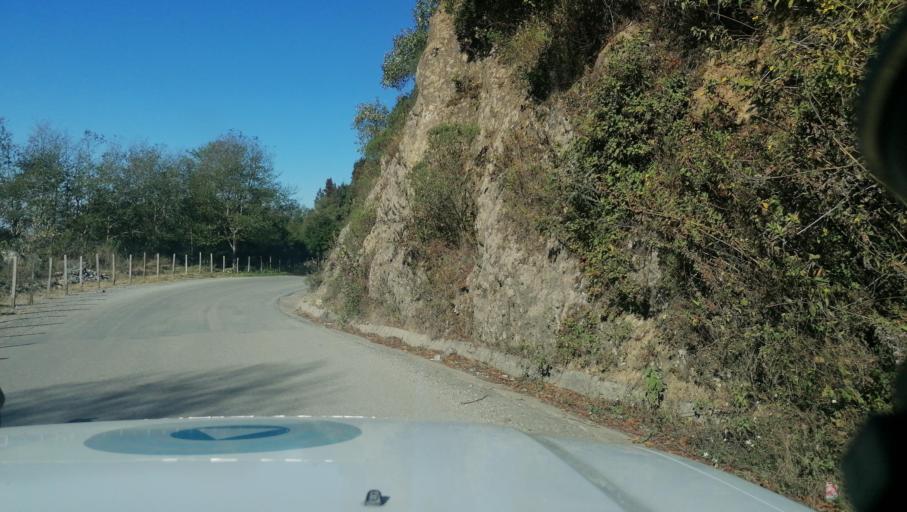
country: MX
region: Chiapas
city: Motozintla de Mendoza
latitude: 15.2665
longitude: -92.2242
